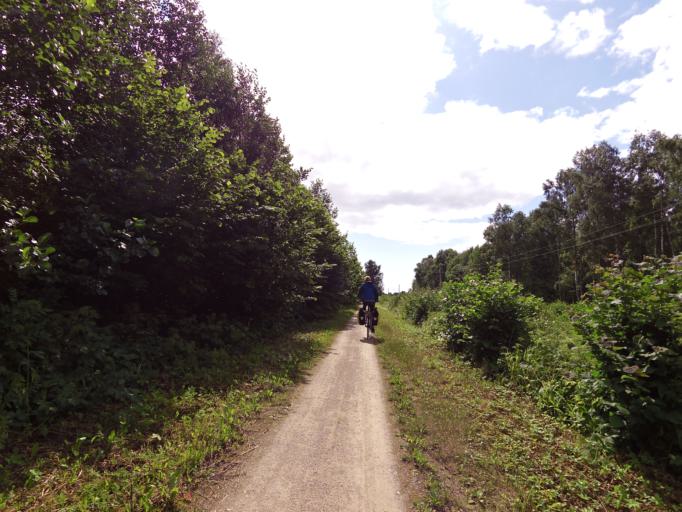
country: EE
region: Laeaene
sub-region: Haapsalu linn
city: Haapsalu
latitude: 58.9146
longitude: 23.4404
